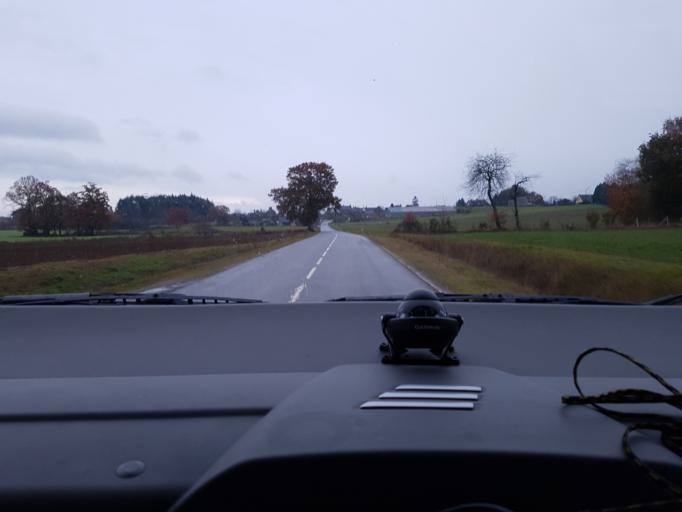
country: FR
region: Brittany
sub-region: Departement d'Ille-et-Vilaine
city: Saint-Marc-le-Blanc
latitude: 48.3599
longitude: -1.3882
